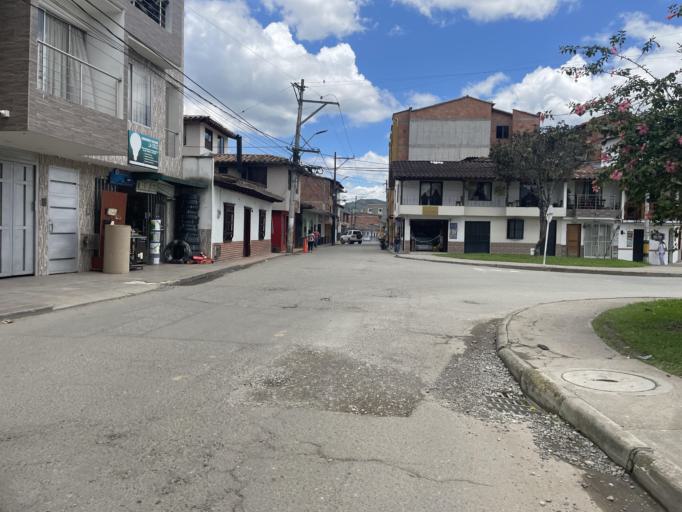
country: CO
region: Antioquia
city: La Ceja
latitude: 6.0226
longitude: -75.4333
